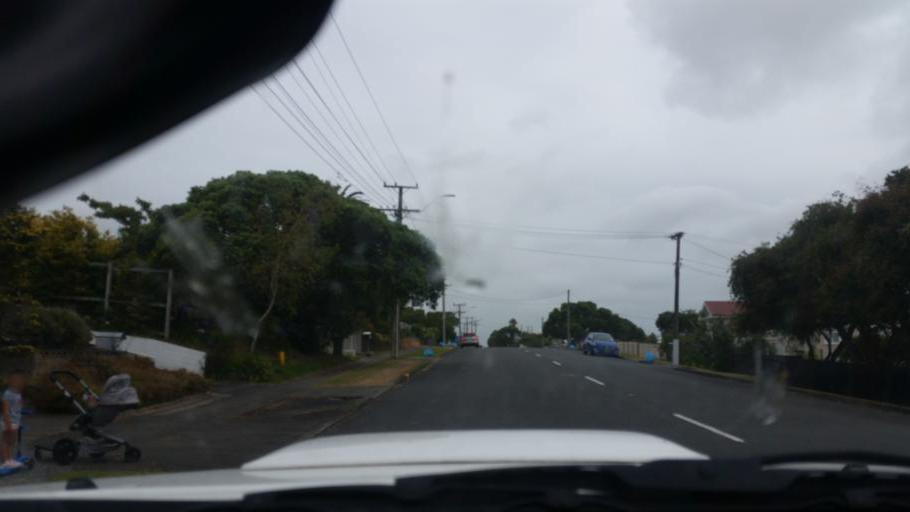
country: NZ
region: Northland
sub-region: Kaipara District
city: Dargaville
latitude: -35.9319
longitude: 173.8715
